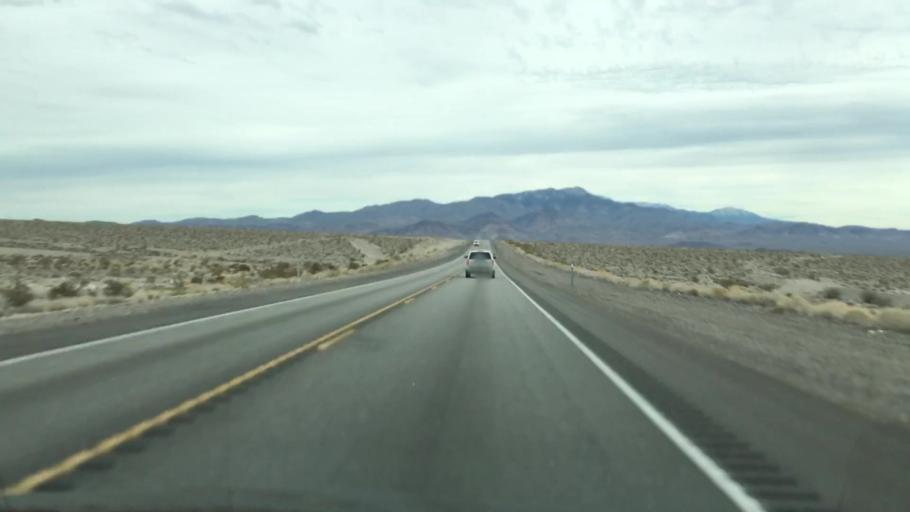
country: US
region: Nevada
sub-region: Nye County
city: Pahrump
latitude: 36.5799
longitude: -116.2001
